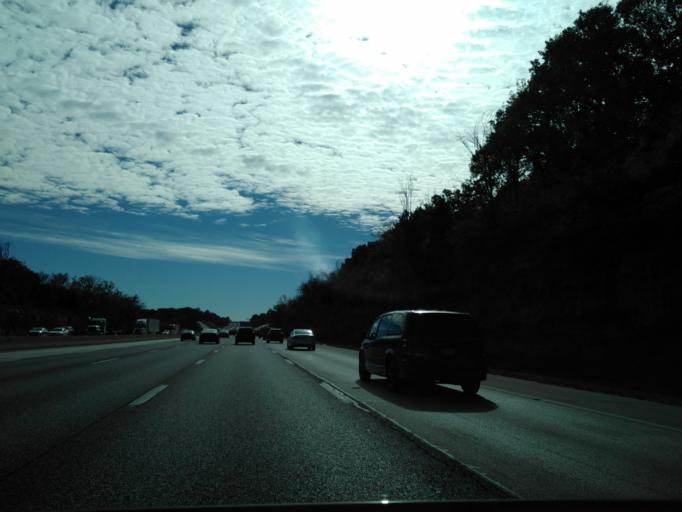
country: US
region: Missouri
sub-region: Saint Louis County
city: Sunset Hills
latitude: 38.5327
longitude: -90.4087
